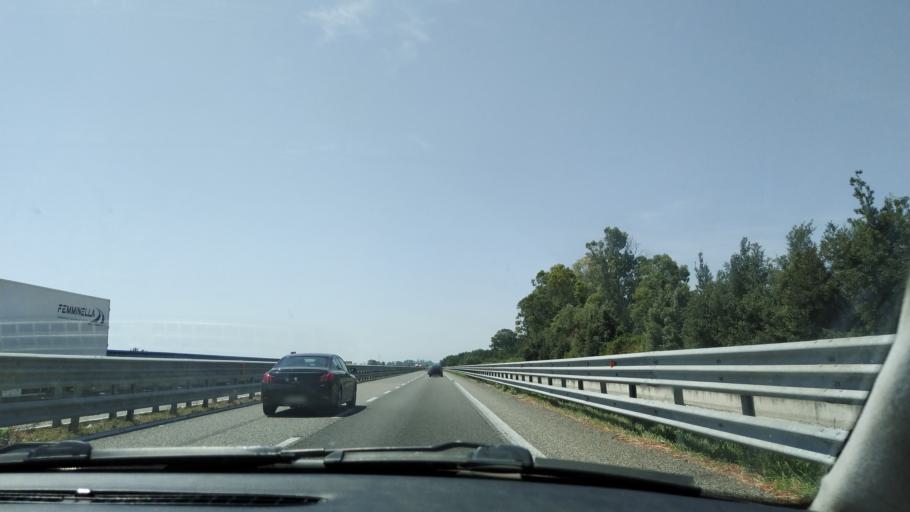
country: IT
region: Basilicate
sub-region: Provincia di Matera
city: Marconia
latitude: 40.3507
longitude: 16.7706
